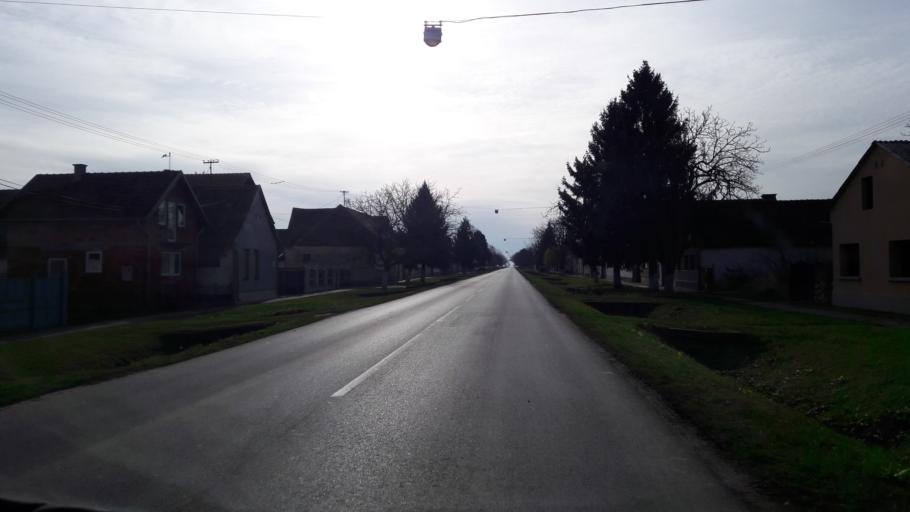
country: HR
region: Osjecko-Baranjska
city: Semeljci
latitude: 45.3507
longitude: 18.5575
